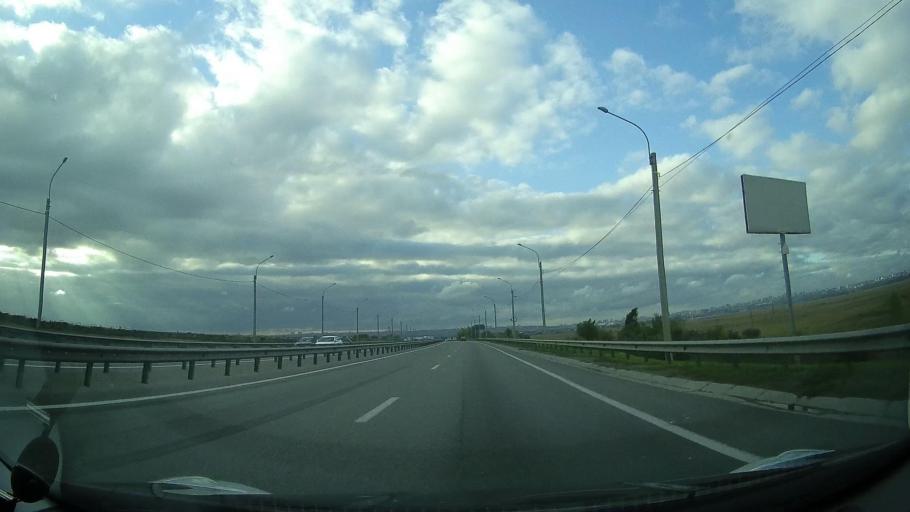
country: RU
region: Rostov
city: Bataysk
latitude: 47.1652
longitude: 39.7573
